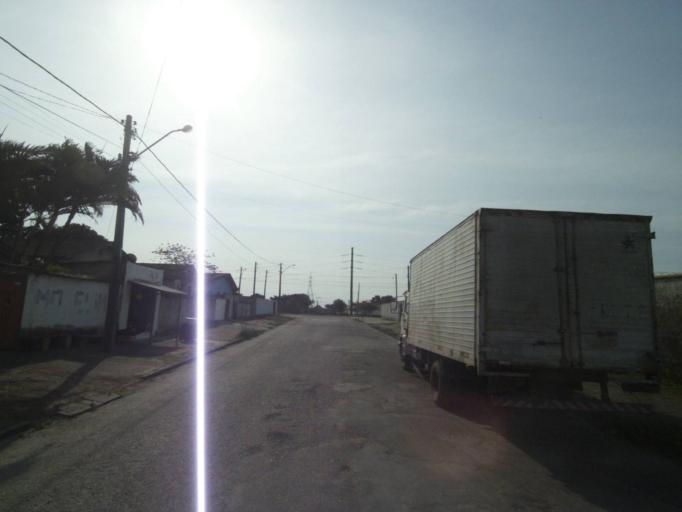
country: BR
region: Parana
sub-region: Paranagua
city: Paranagua
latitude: -25.5365
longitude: -48.5334
